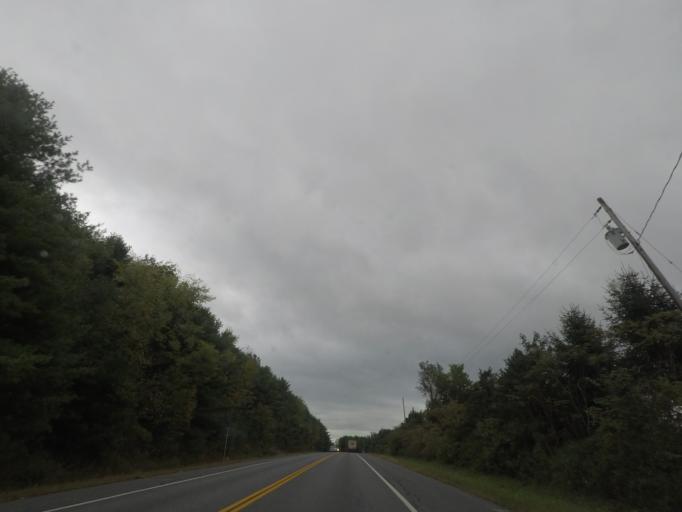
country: US
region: New York
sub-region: Rensselaer County
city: Hoosick Falls
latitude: 42.9494
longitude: -73.3728
